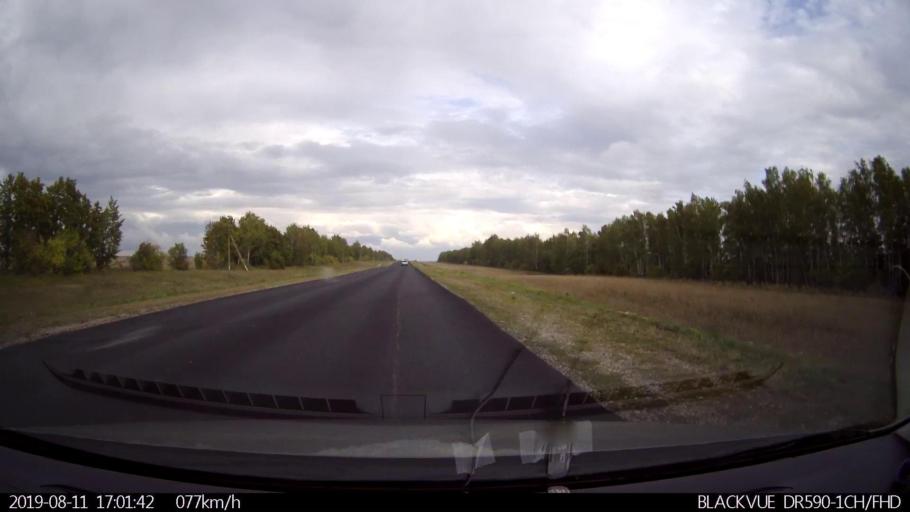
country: RU
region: Ulyanovsk
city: Mayna
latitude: 54.3076
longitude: 47.7022
